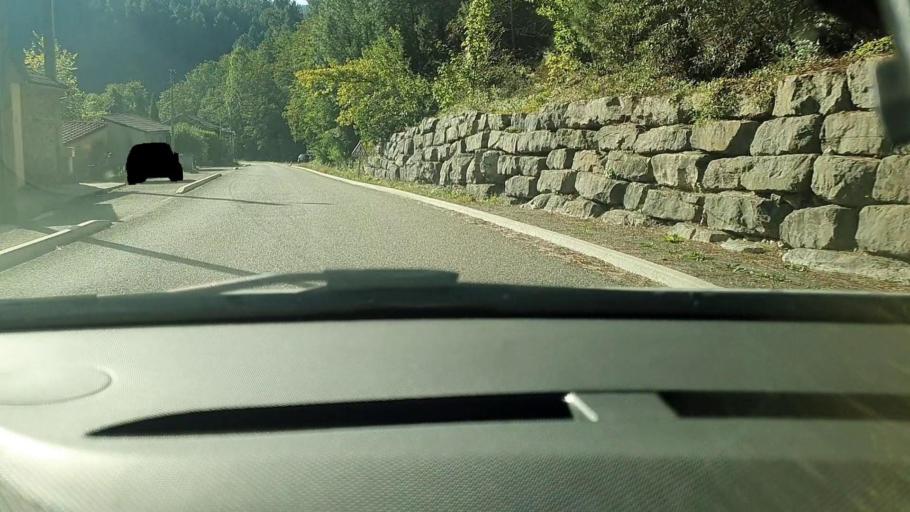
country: FR
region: Languedoc-Roussillon
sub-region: Departement du Gard
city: Besseges
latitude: 44.2986
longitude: 4.0621
